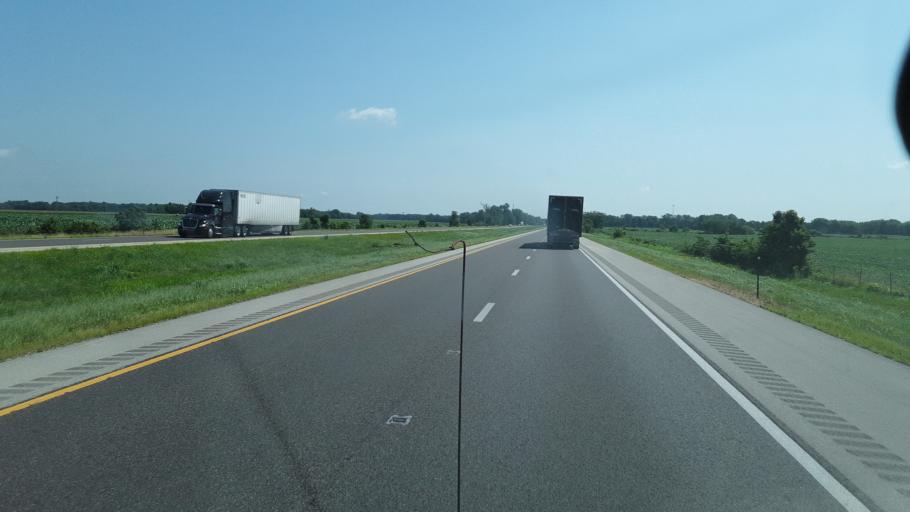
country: US
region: Illinois
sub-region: Cumberland County
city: Toledo
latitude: 39.1903
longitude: -88.3277
